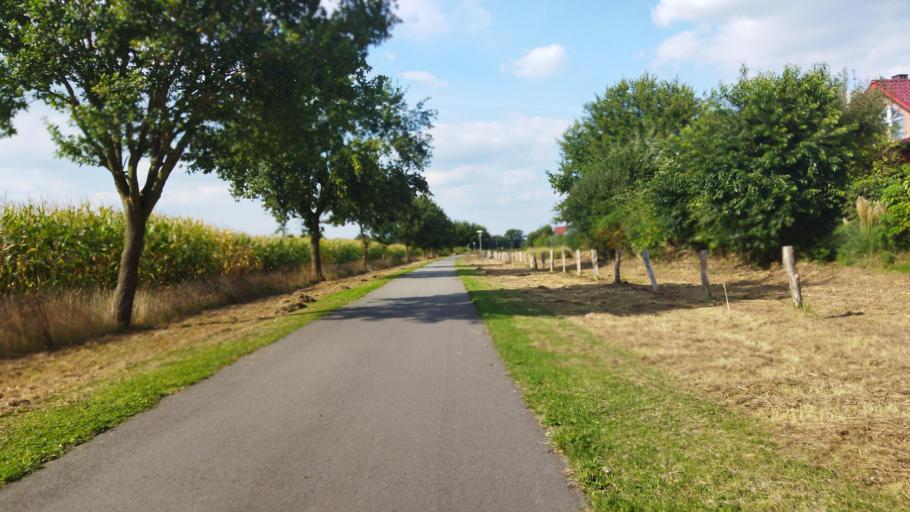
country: DE
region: Lower Saxony
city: Walchum
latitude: 52.9293
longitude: 7.2892
